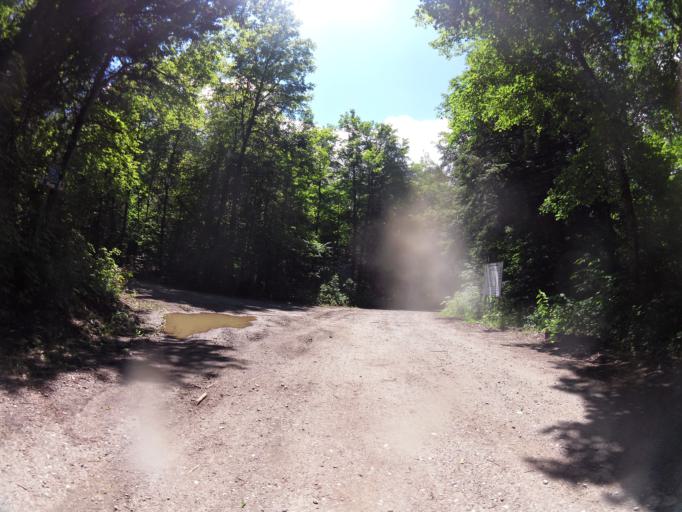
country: CA
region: Ontario
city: Perth
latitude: 45.0228
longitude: -76.6342
